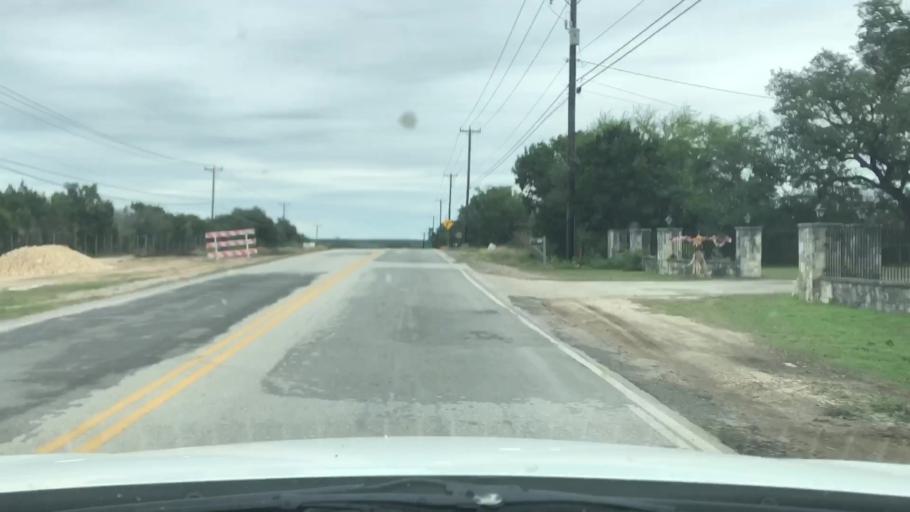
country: US
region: Texas
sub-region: Bexar County
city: Timberwood Park
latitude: 29.6481
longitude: -98.4202
